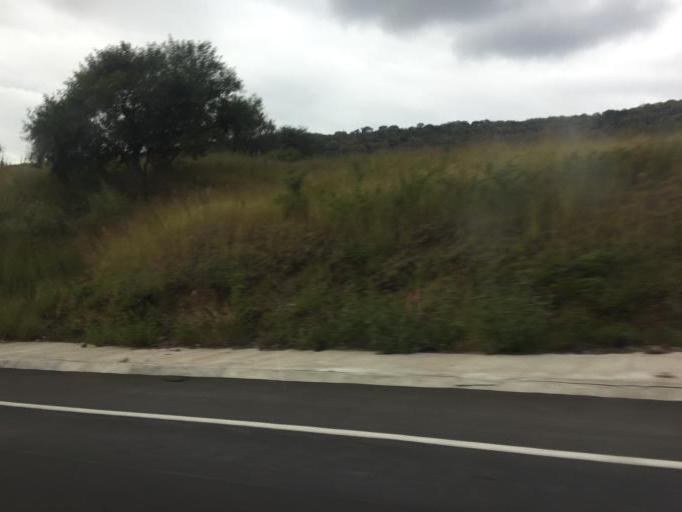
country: MX
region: Jalisco
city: Ocotlan
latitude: 20.4201
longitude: -102.7616
